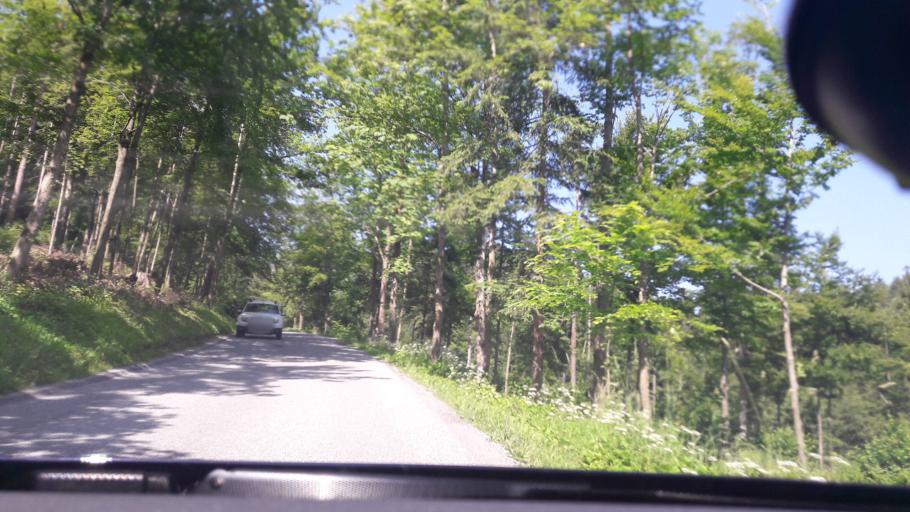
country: AT
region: Styria
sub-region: Politischer Bezirk Voitsberg
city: Sodingberg
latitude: 47.1124
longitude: 15.1571
